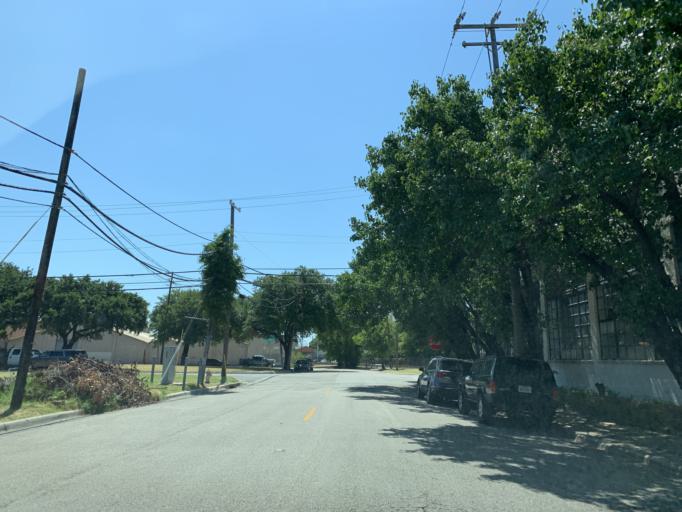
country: US
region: Texas
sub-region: Dallas County
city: Dallas
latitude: 32.7863
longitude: -96.7726
